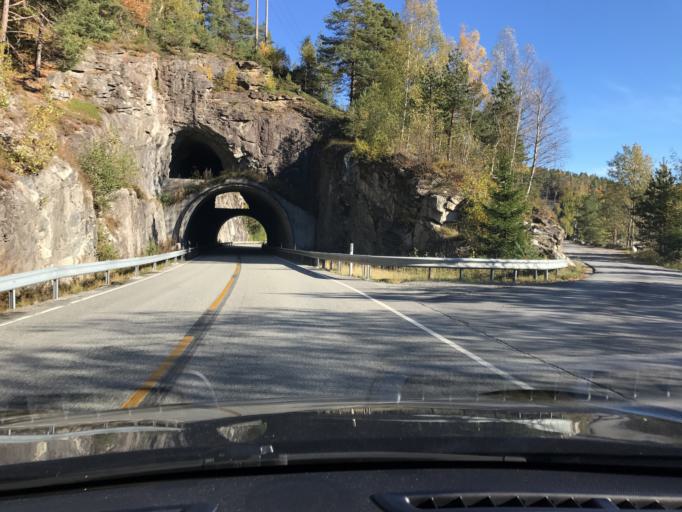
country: NO
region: Buskerud
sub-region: Fla
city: Fla
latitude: 60.3875
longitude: 9.5875
